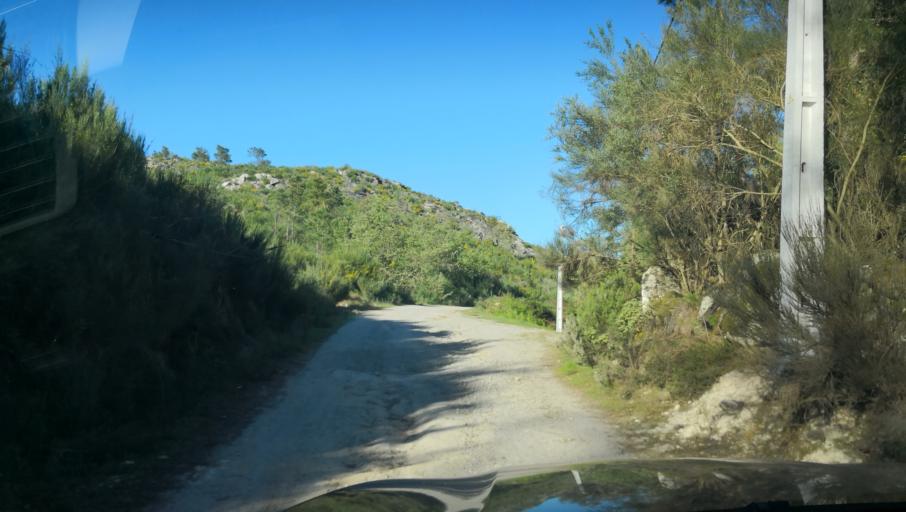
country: PT
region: Vila Real
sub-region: Vila Real
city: Vila Real
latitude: 41.3312
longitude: -7.6812
